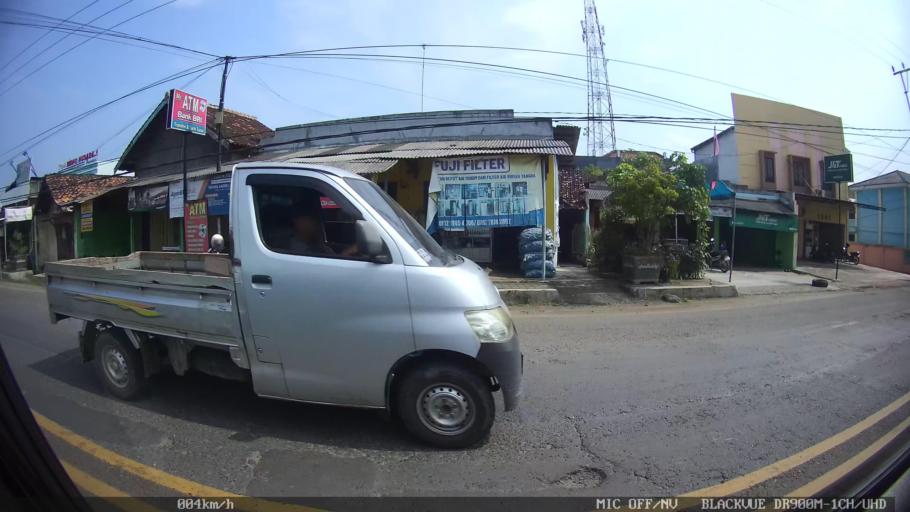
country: ID
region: Lampung
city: Gedongtataan
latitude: -5.3800
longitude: 105.0990
